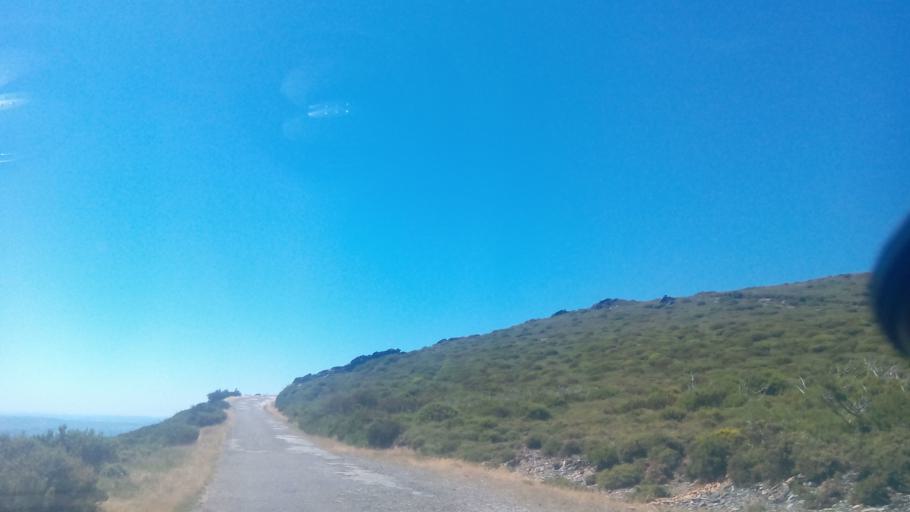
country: PT
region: Vila Real
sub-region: Mesao Frio
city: Mesao Frio
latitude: 41.2543
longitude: -7.8971
